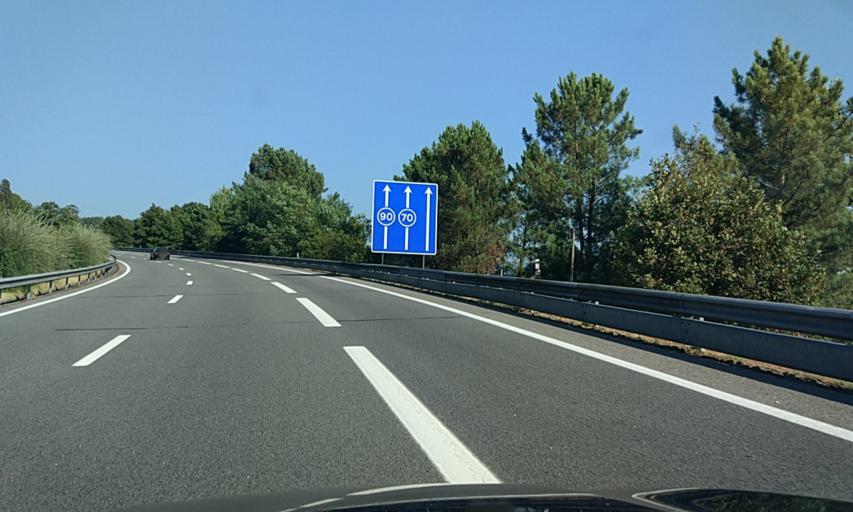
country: PT
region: Porto
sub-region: Marco de Canaveses
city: Marco de Canavezes
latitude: 41.2261
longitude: -8.1561
